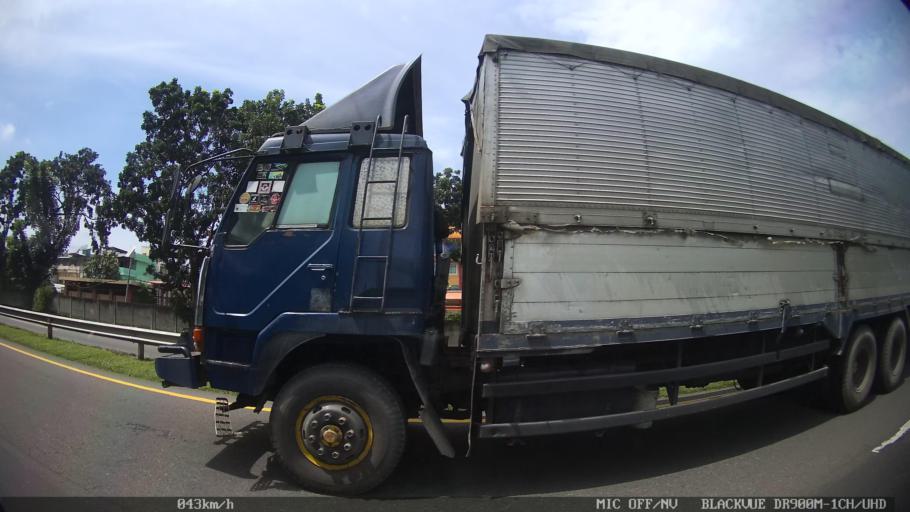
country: ID
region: North Sumatra
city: Medan
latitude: 3.6395
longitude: 98.7007
